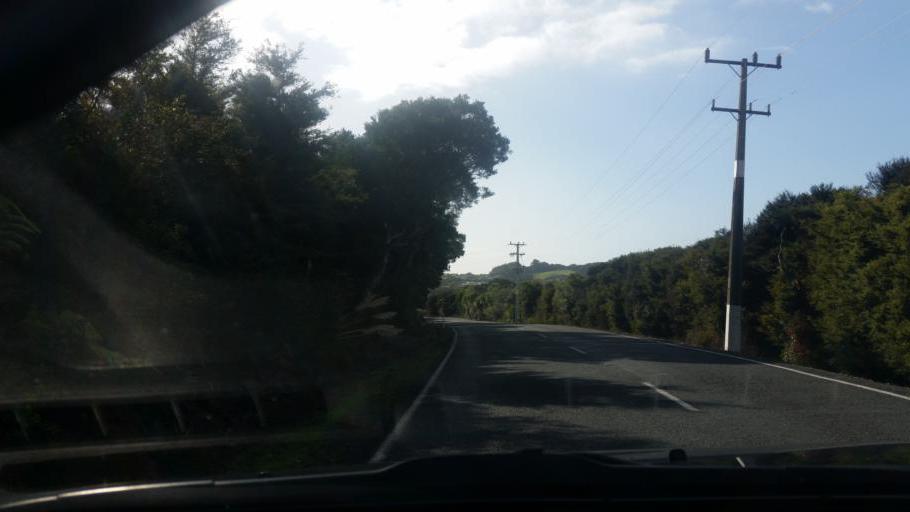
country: NZ
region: Auckland
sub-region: Auckland
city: Wellsford
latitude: -36.0972
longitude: 174.5602
